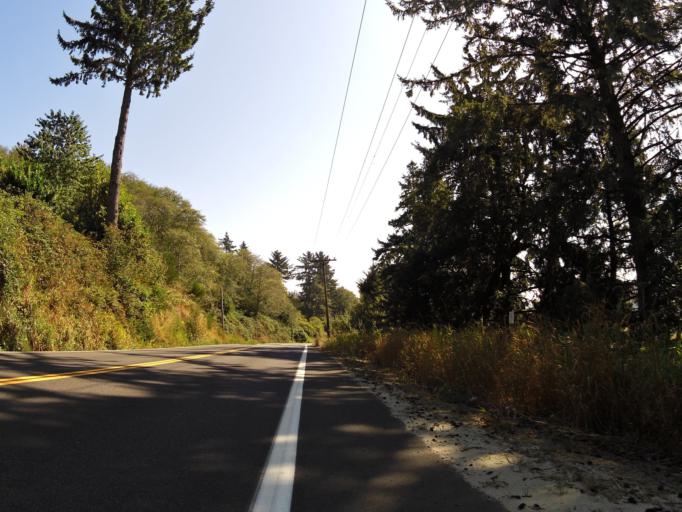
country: US
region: Oregon
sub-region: Tillamook County
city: Pacific City
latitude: 45.1882
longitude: -123.9481
